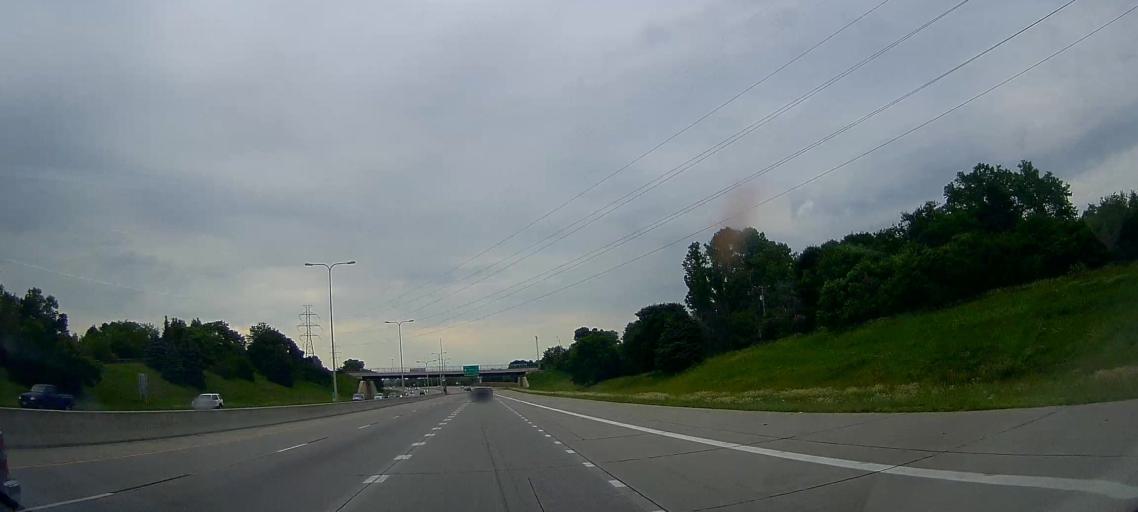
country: US
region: Nebraska
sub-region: Douglas County
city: Ralston
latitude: 41.2943
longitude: -96.0723
